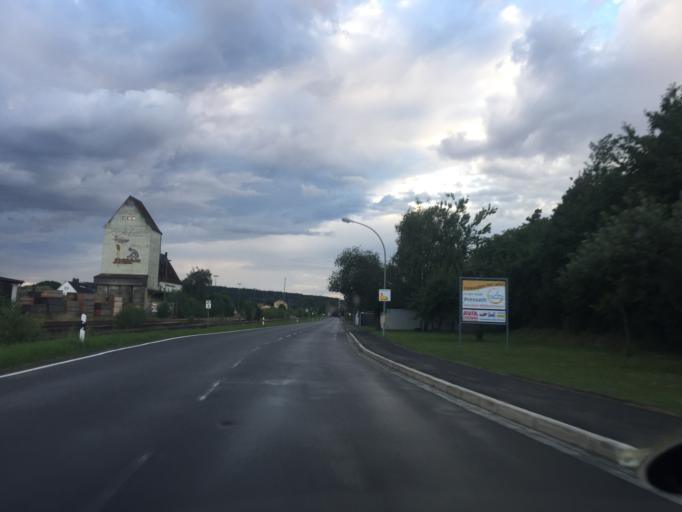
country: DE
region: Bavaria
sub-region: Upper Palatinate
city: Pressath
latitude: 49.7615
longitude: 11.9447
